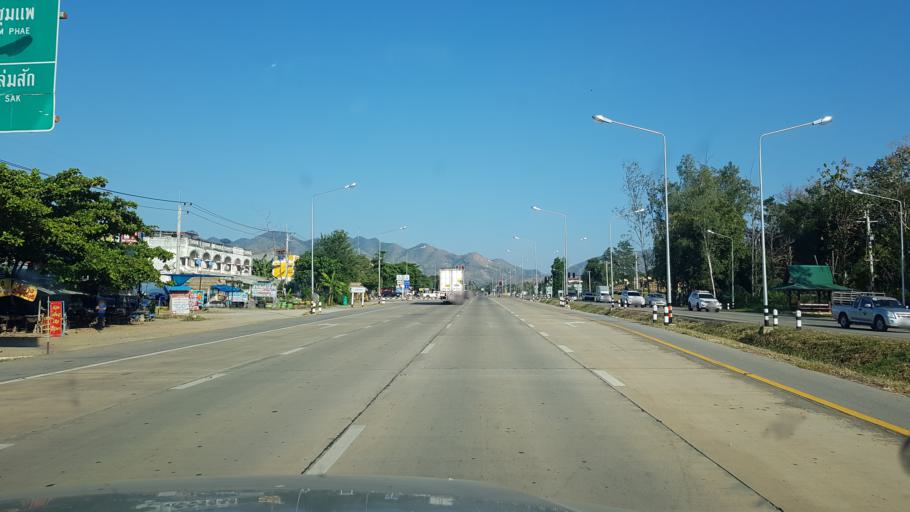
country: TH
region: Phetchabun
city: Lom Sak
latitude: 16.7284
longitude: 101.2835
